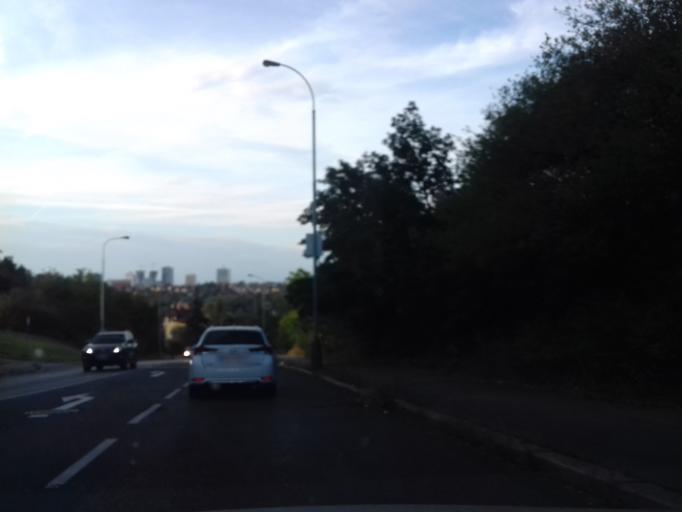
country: CZ
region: Praha
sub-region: Praha 4
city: Hodkovicky
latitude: 50.0298
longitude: 14.4505
